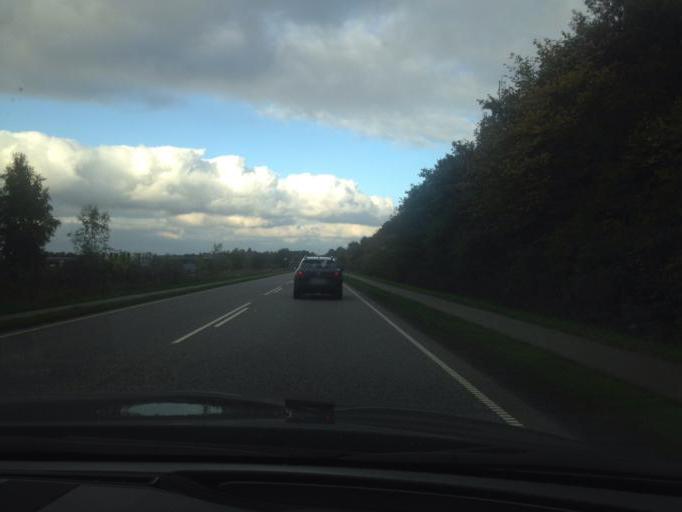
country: DK
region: South Denmark
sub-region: Kolding Kommune
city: Kolding
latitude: 55.5356
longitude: 9.4709
